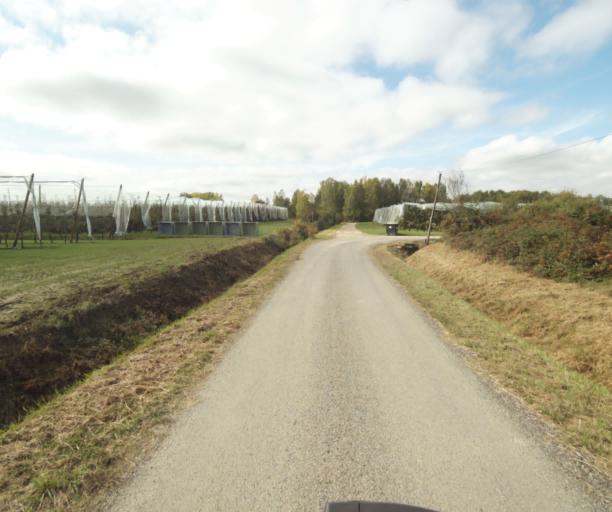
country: FR
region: Midi-Pyrenees
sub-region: Departement du Tarn-et-Garonne
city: Finhan
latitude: 43.9268
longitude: 1.1995
